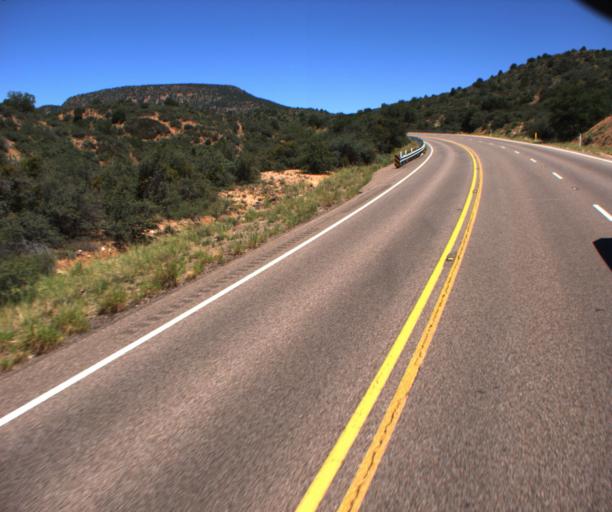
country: US
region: Arizona
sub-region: Gila County
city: Globe
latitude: 33.6309
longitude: -110.5832
